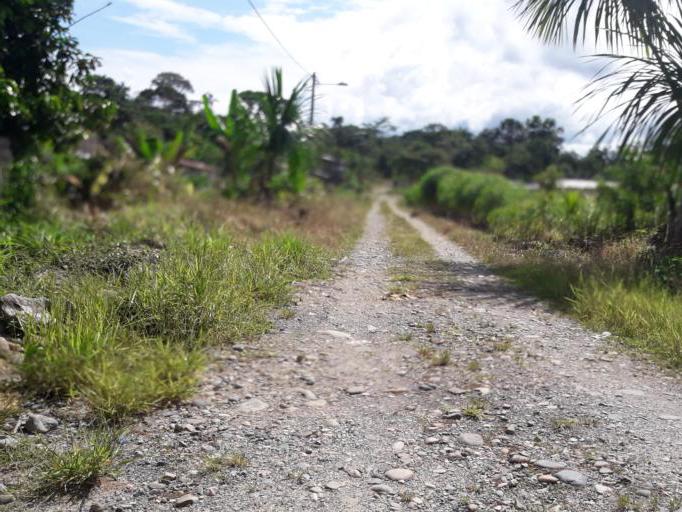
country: EC
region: Napo
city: Tena
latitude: -0.9559
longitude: -77.8254
